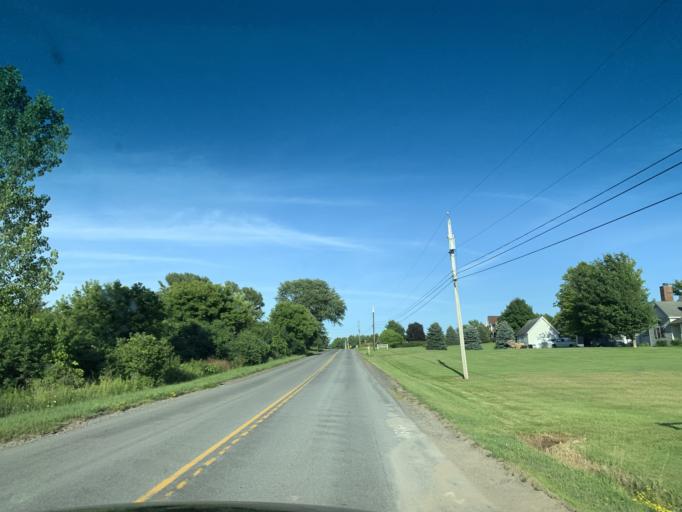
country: US
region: New York
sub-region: Oneida County
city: Clinton
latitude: 43.0546
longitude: -75.4524
